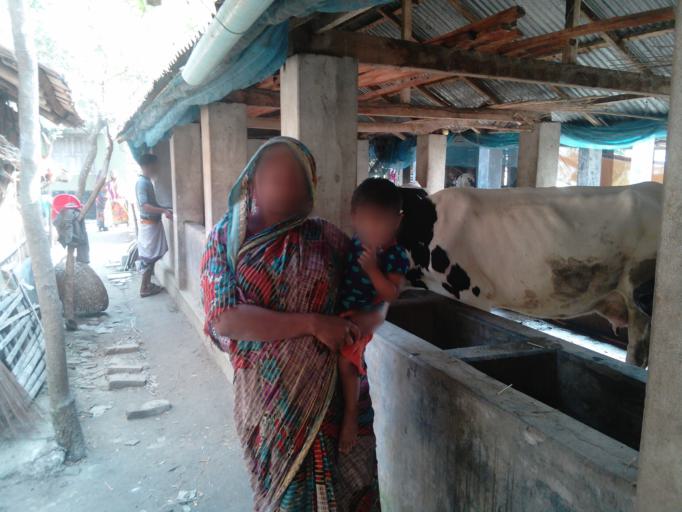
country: BD
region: Khulna
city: Kesabpur
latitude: 22.7813
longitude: 89.2748
